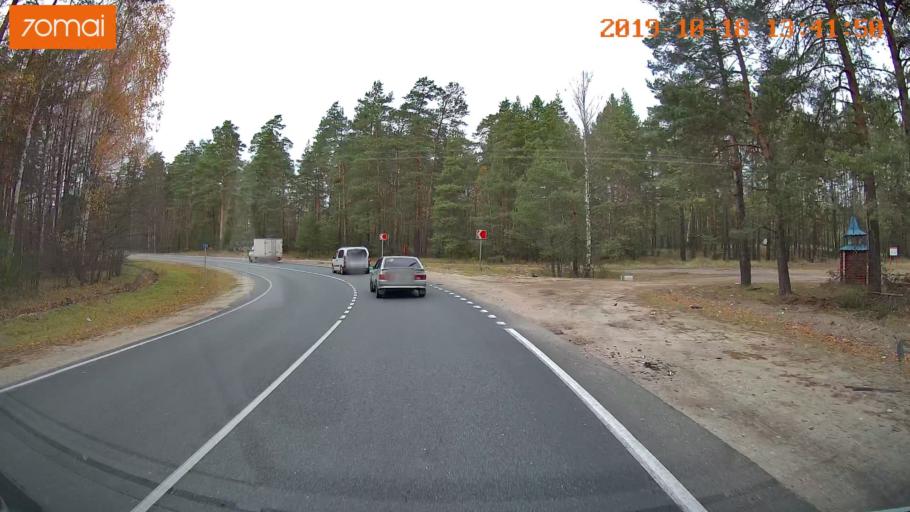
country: RU
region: Rjazan
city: Solotcha
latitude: 54.9240
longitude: 39.9965
